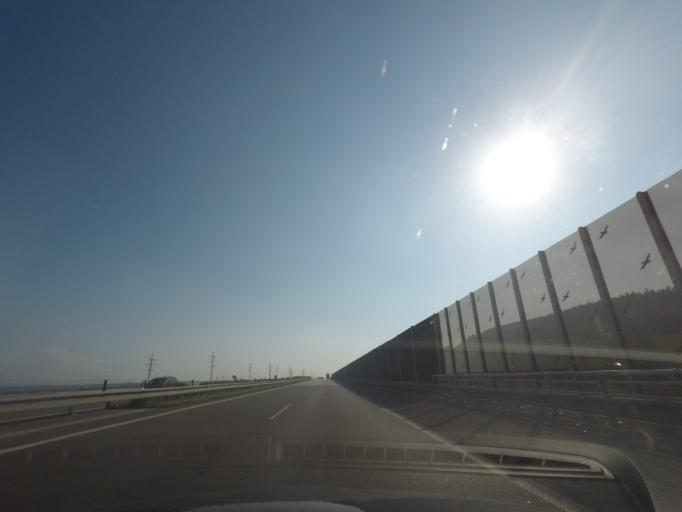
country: CZ
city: Fulnek
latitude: 49.6629
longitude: 17.9098
